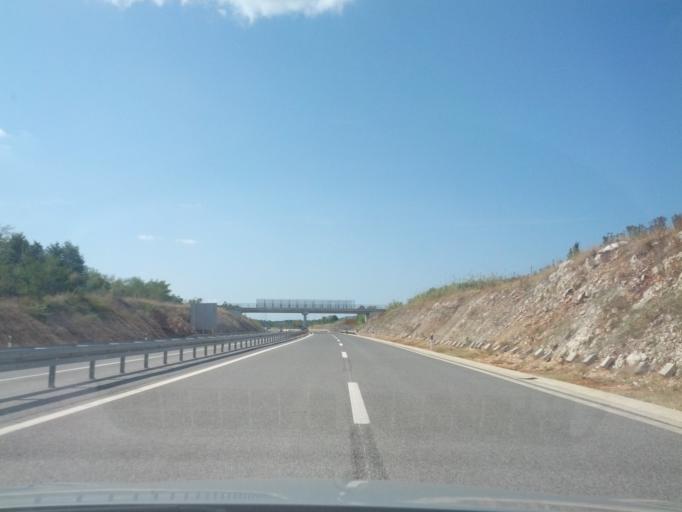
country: HR
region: Istarska
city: Karojba
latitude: 45.2247
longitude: 13.7221
